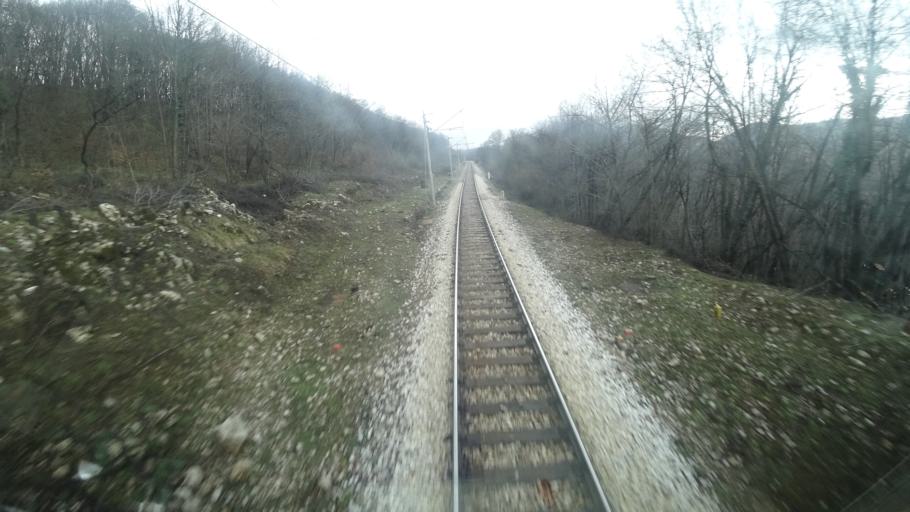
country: HR
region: Primorsko-Goranska
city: Hreljin
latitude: 45.2956
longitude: 14.6422
